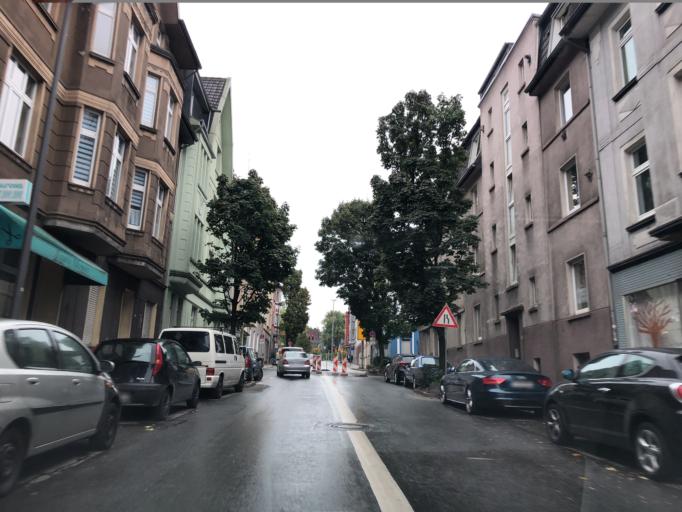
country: DE
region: North Rhine-Westphalia
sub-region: Regierungsbezirk Munster
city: Gelsenkirchen
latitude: 51.4662
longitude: 7.0784
